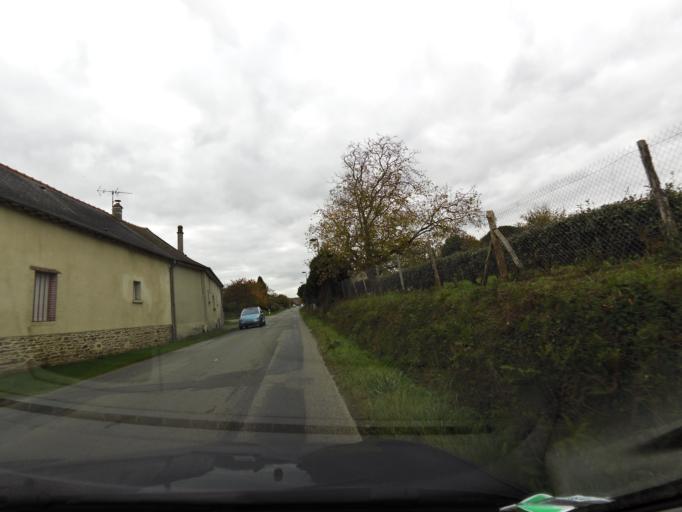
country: FR
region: Brittany
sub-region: Departement d'Ille-et-Vilaine
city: Chanteloup
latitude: 47.9664
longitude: -1.6080
